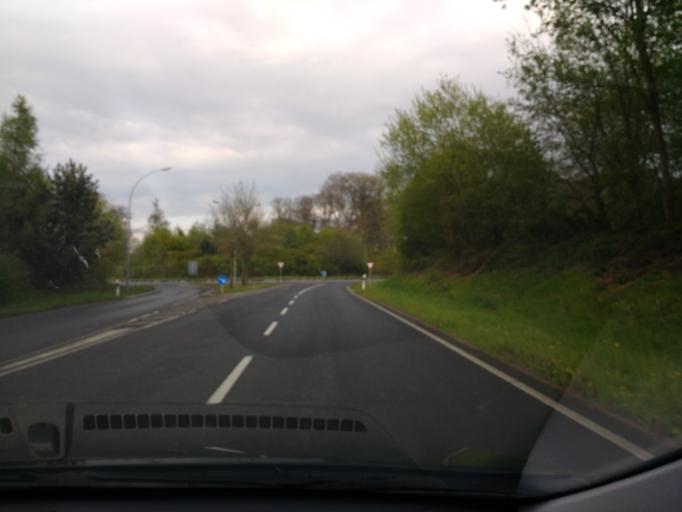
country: LU
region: Luxembourg
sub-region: Canton de Luxembourg
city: Sandweiler
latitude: 49.6089
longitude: 6.2288
